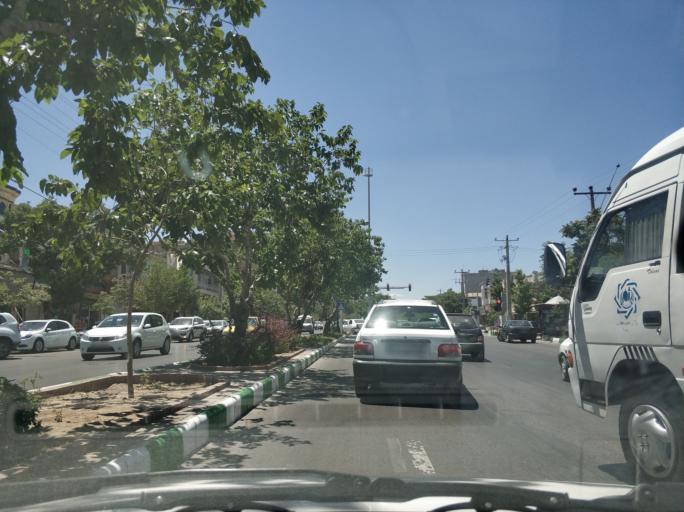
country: IR
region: Razavi Khorasan
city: Mashhad
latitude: 36.3148
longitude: 59.4853
